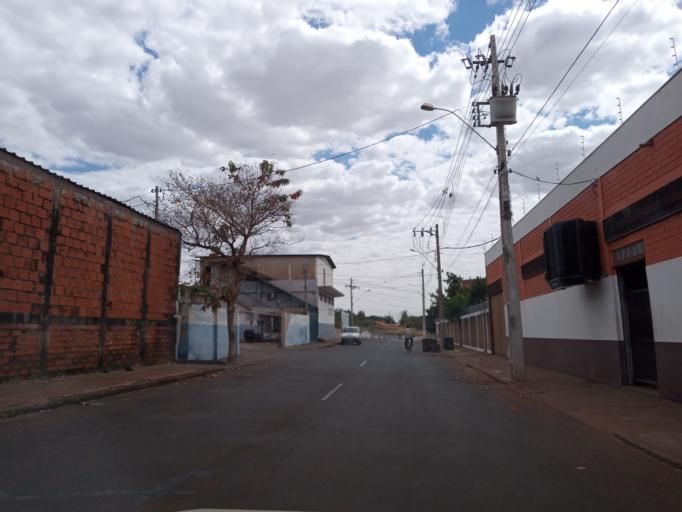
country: BR
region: Minas Gerais
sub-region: Ituiutaba
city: Ituiutaba
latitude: -18.9554
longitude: -49.4561
